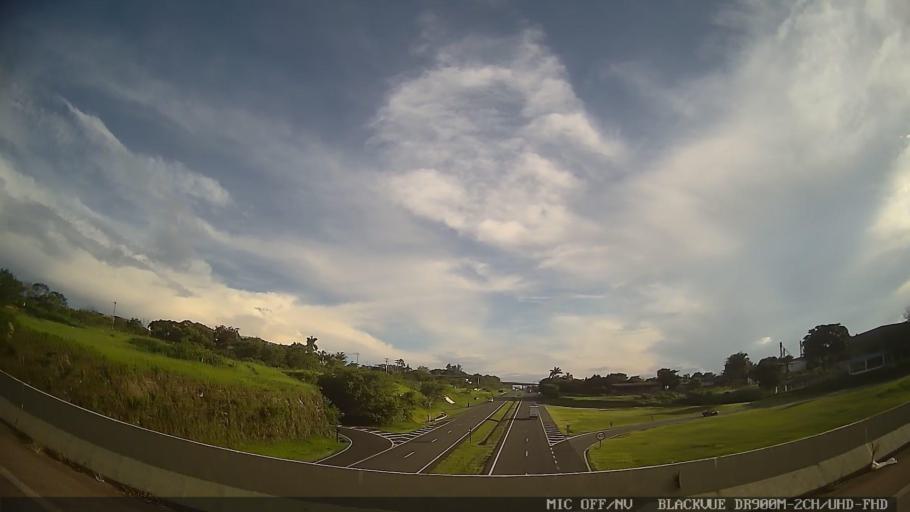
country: BR
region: Sao Paulo
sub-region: Tiete
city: Tiete
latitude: -23.1184
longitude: -47.7176
